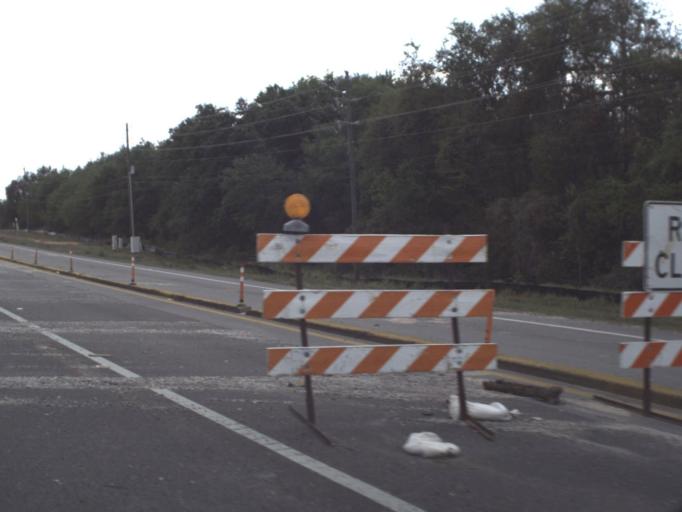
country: US
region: Florida
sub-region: Lake County
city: Clermont
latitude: 28.4717
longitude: -81.7166
